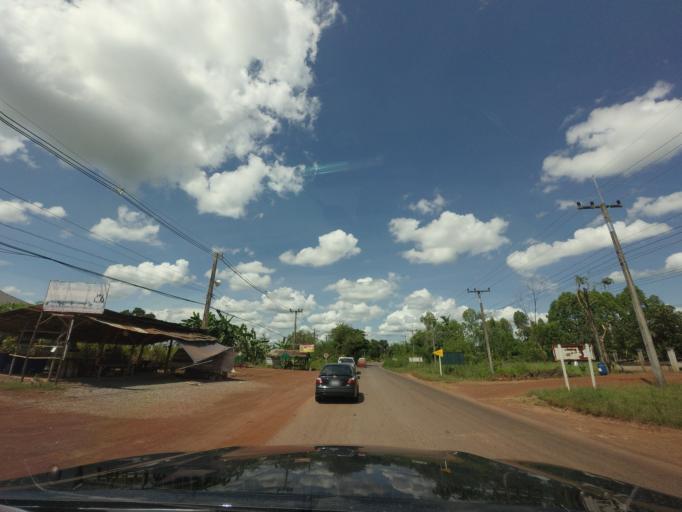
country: TH
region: Changwat Udon Thani
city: Ban Dung
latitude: 17.7350
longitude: 103.2533
